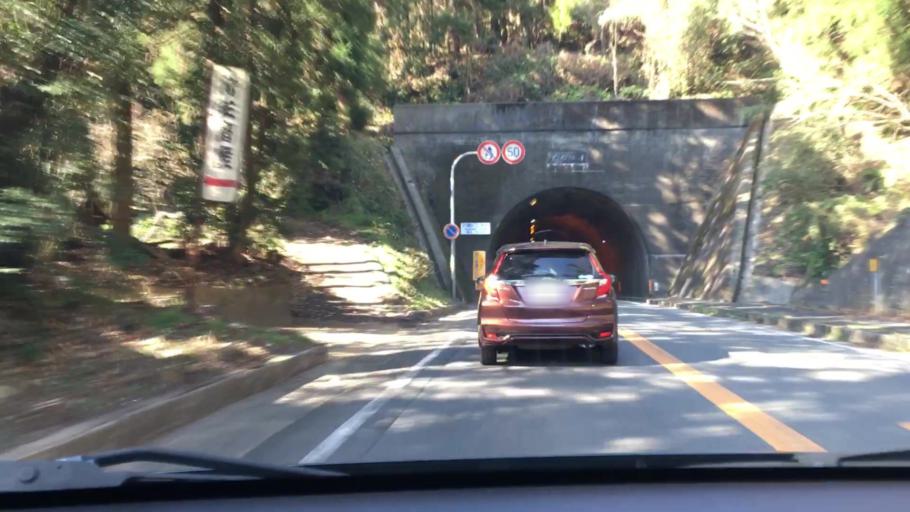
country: JP
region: Oita
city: Saiki
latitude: 32.9913
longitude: 131.8304
